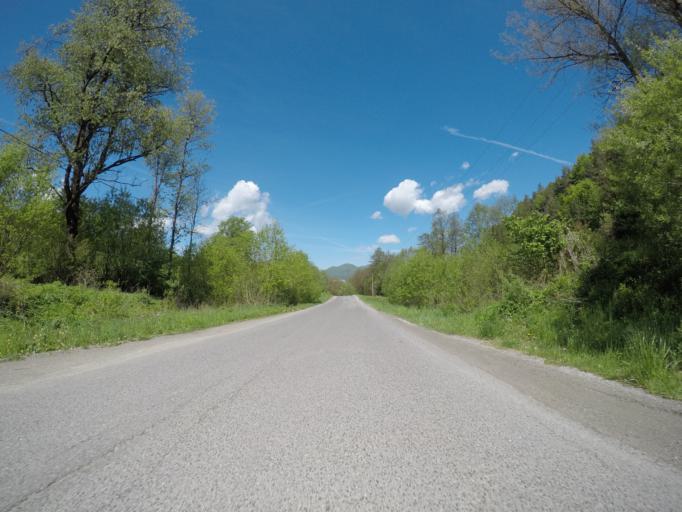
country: SK
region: Banskobystricky
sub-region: Okres Banska Bystrica
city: Banska Bystrica
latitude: 48.7320
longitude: 19.2048
